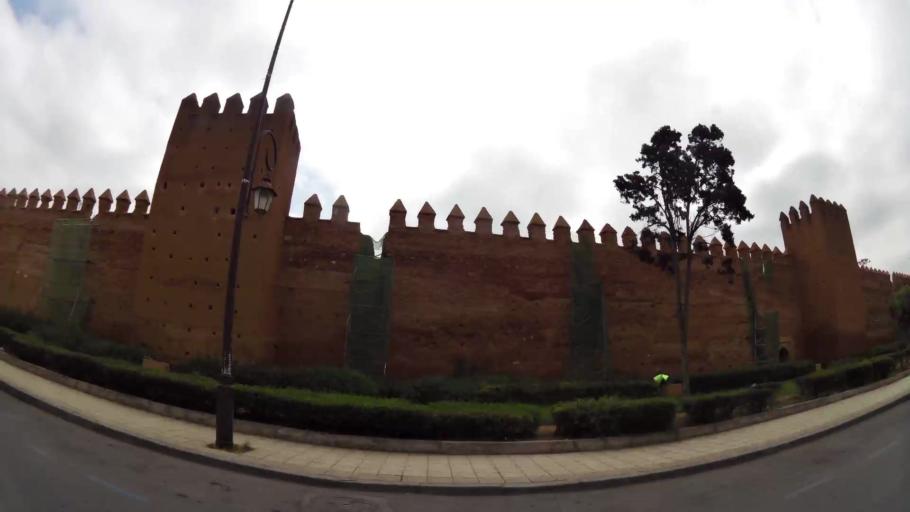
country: MA
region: Rabat-Sale-Zemmour-Zaer
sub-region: Rabat
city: Rabat
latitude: 34.0195
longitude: -6.8399
